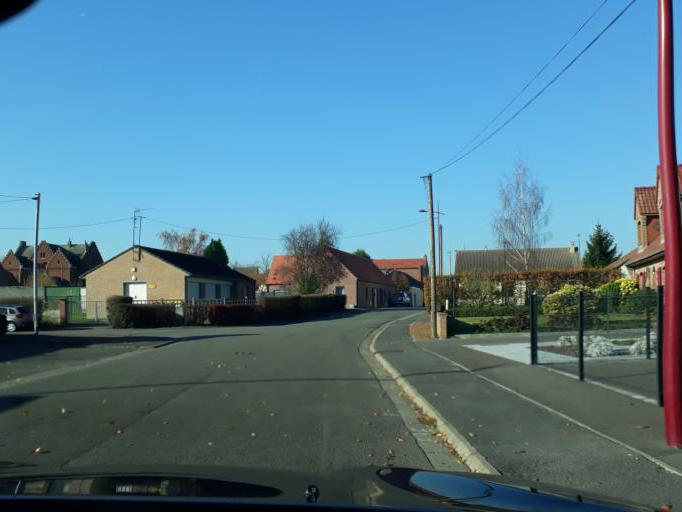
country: FR
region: Nord-Pas-de-Calais
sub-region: Departement du Nord
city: Masny
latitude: 50.3482
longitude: 3.2032
